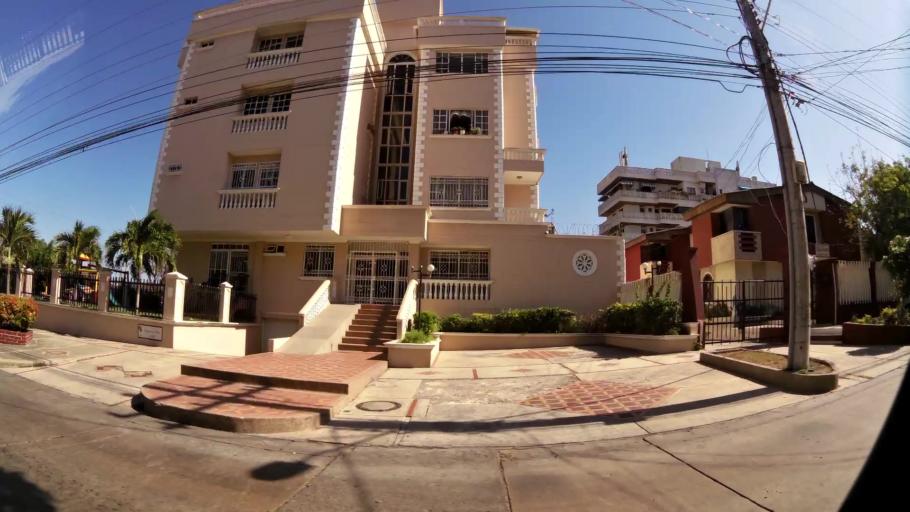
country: CO
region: Atlantico
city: Barranquilla
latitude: 10.9989
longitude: -74.7958
